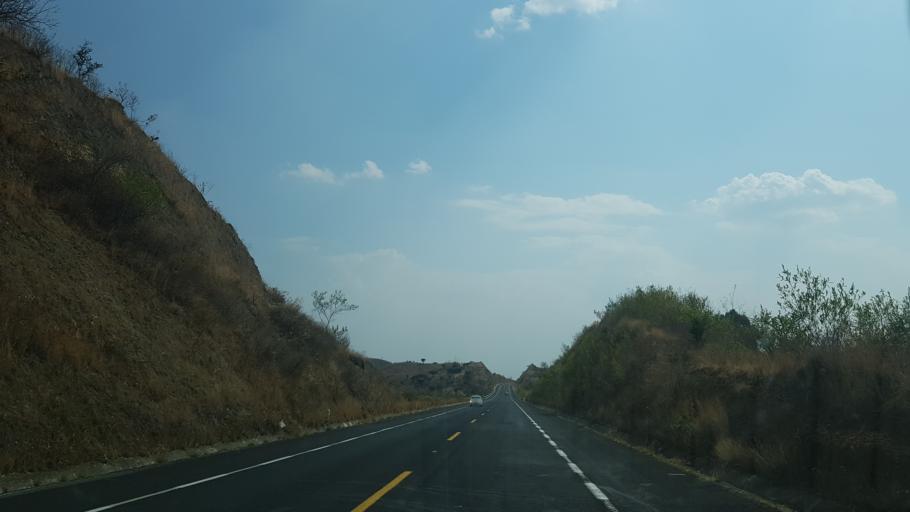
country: MX
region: Morelos
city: Tlacotepec
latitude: 18.8058
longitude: -98.7058
